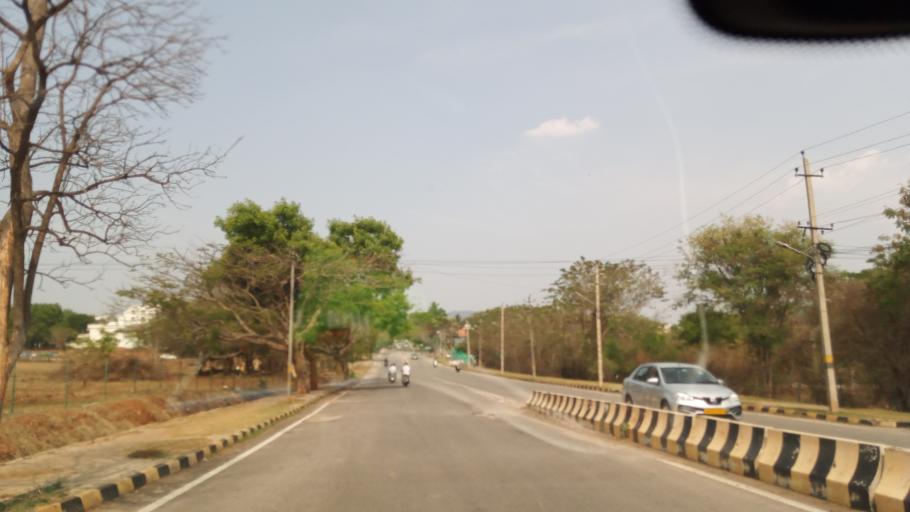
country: IN
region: Karnataka
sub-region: Mysore
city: Mysore
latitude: 12.2873
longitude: 76.6177
